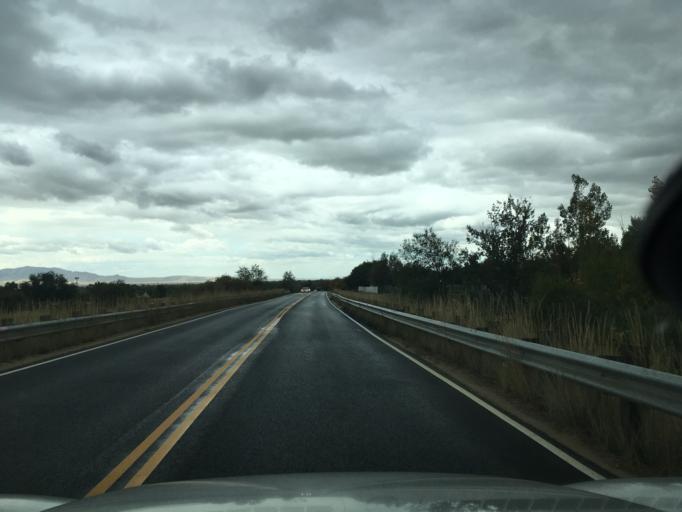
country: US
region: Utah
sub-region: Davis County
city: Kaysville
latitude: 41.0625
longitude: -111.9345
